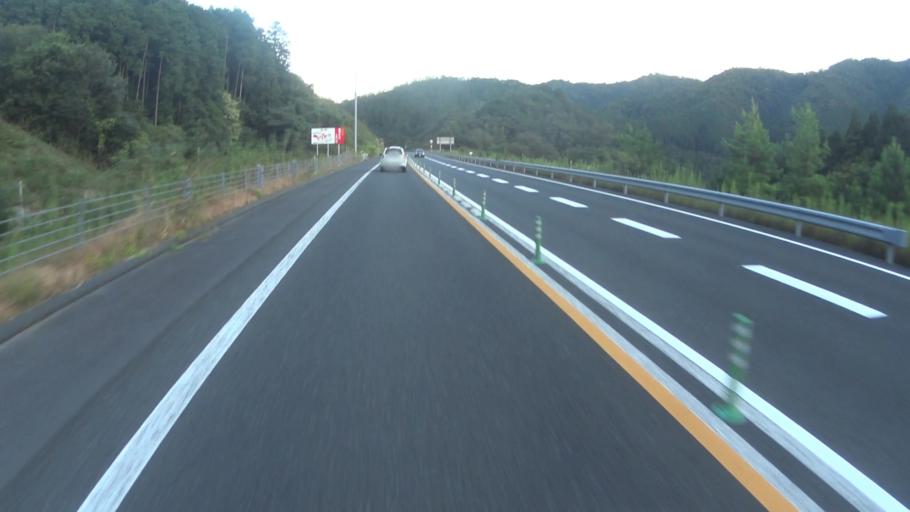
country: JP
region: Kyoto
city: Miyazu
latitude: 35.4410
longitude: 135.1918
